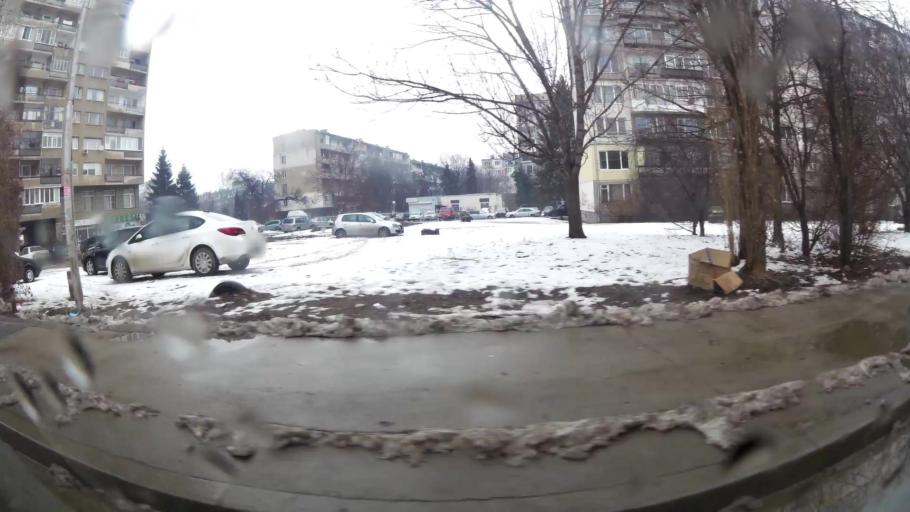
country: BG
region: Sofia-Capital
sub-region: Stolichna Obshtina
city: Sofia
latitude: 42.6681
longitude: 23.2802
